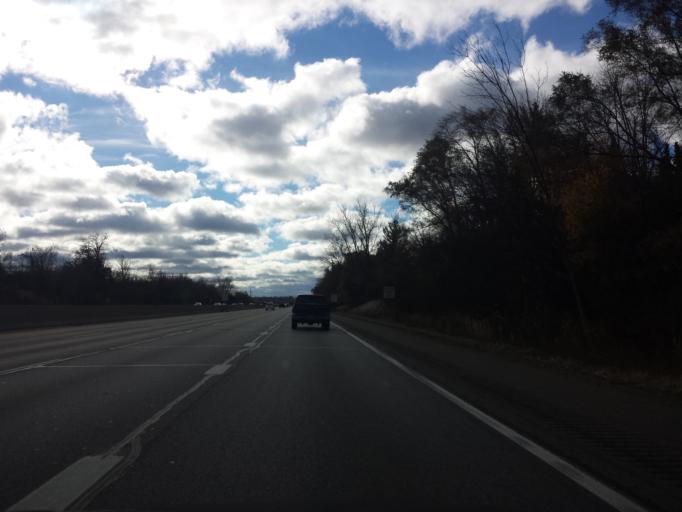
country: US
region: Michigan
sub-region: Oakland County
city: Bloomfield Hills
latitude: 42.6282
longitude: -83.2382
